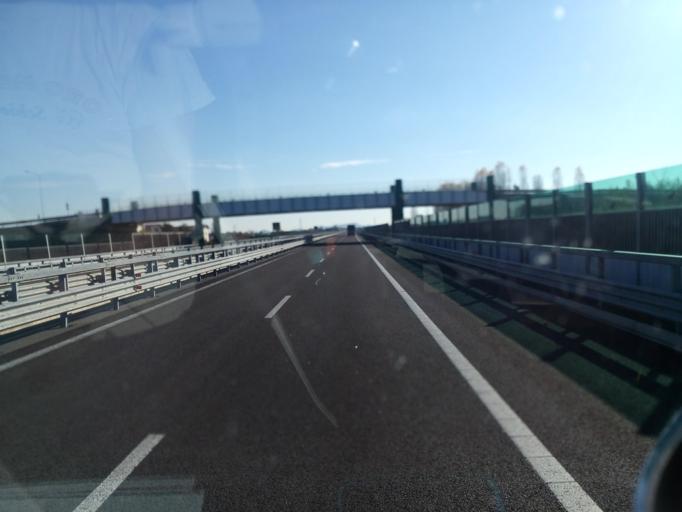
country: IT
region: Veneto
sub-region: Provincia di Vicenza
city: Longare
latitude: 45.4868
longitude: 11.6243
